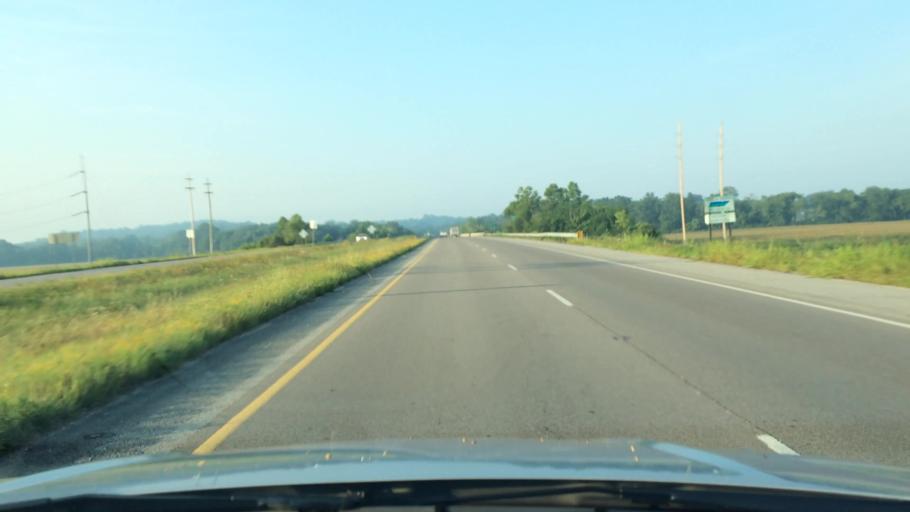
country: US
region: Tennessee
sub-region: Giles County
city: Pulaski
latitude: 35.2017
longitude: -87.0633
